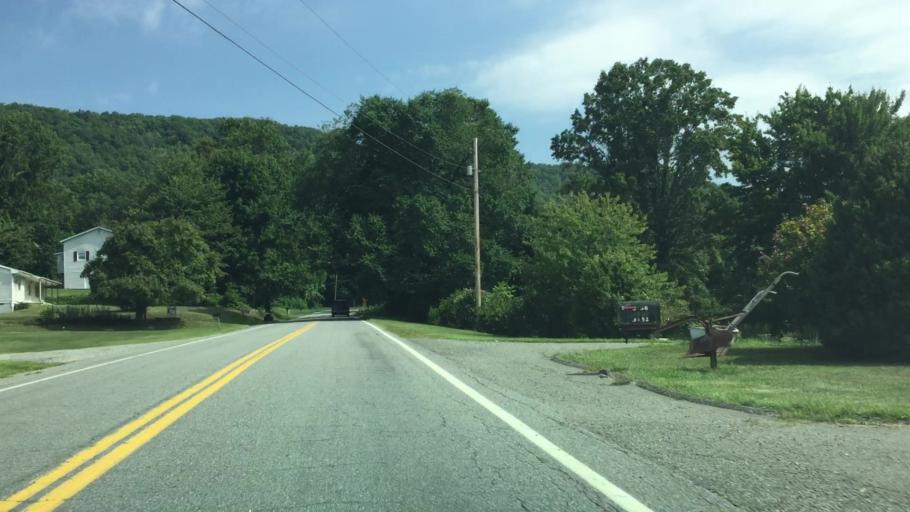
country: US
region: Virginia
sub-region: Pulaski County
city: Pulaski
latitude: 37.0053
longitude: -80.7992
